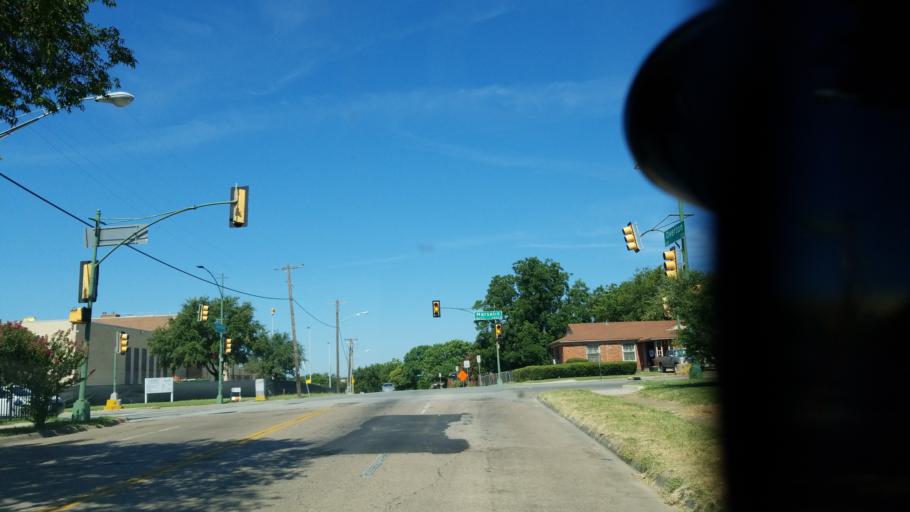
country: US
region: Texas
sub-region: Dallas County
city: Cockrell Hill
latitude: 32.7008
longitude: -96.8142
